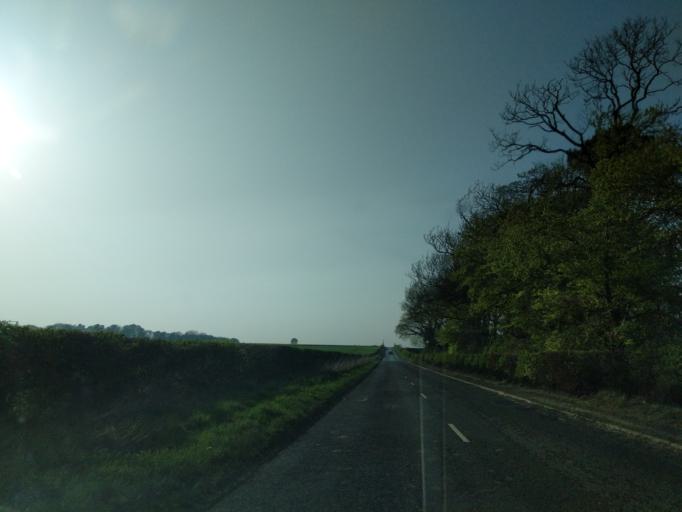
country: GB
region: Scotland
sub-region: Fife
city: Pathhead
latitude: 55.8798
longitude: -3.0141
